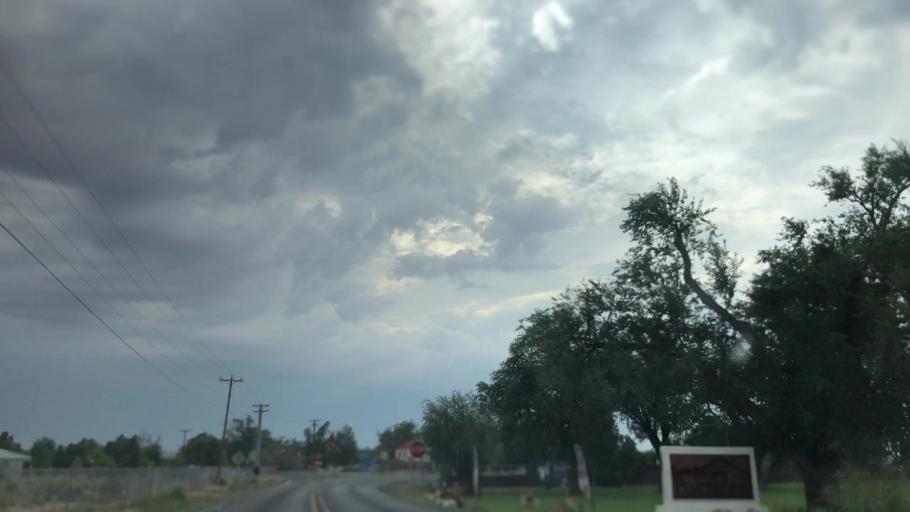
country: US
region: Texas
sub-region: El Paso County
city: Canutillo
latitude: 31.9186
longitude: -106.6248
